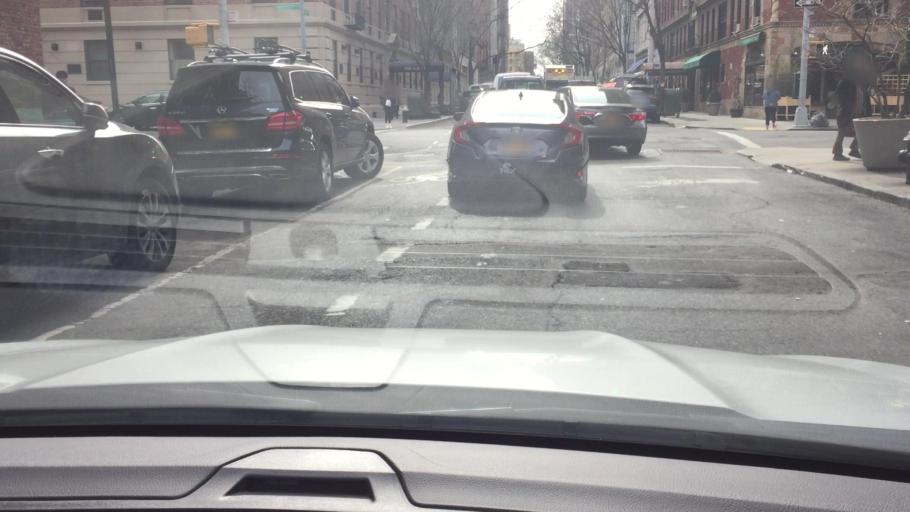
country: US
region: New York
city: New York City
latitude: 40.7328
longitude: -73.9942
